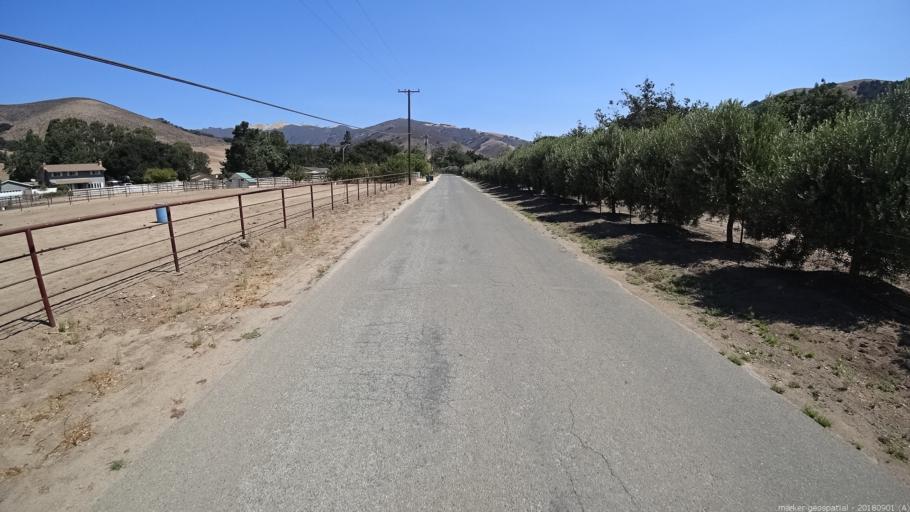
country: US
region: California
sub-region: Monterey County
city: Chualar
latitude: 36.6007
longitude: -121.4326
